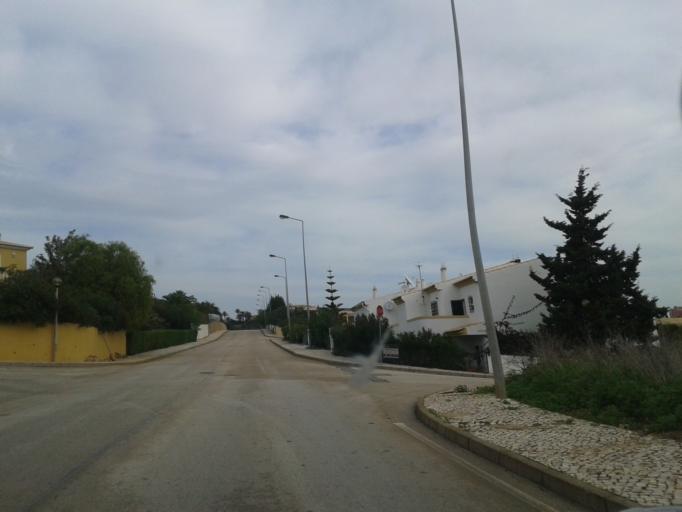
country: PT
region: Faro
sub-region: Lagos
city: Lagos
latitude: 37.0882
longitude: -8.7367
